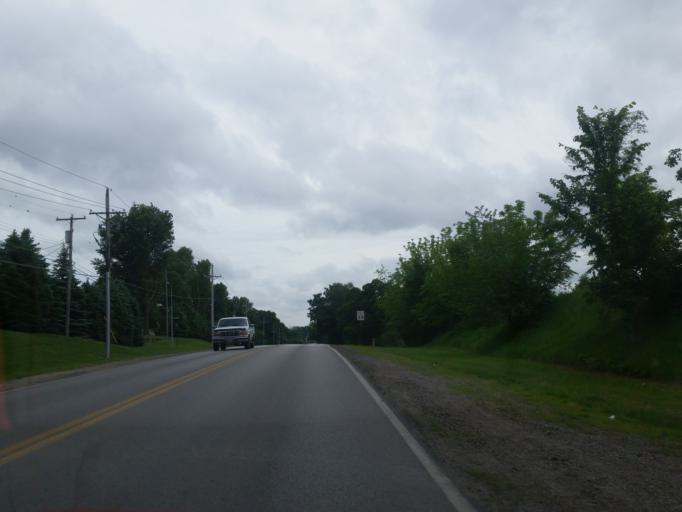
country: US
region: Nebraska
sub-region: Sarpy County
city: Offutt Air Force Base
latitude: 41.1211
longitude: -95.9666
